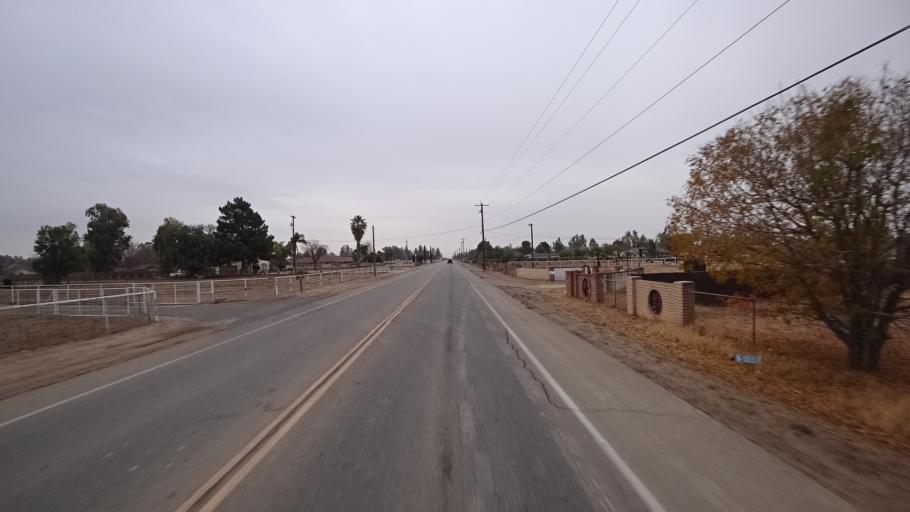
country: US
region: California
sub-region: Kern County
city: Lamont
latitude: 35.3321
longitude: -118.9321
